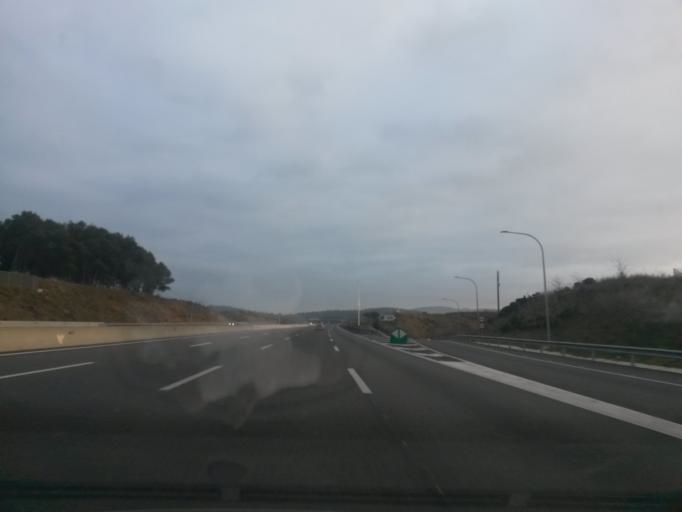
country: ES
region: Catalonia
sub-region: Provincia de Girona
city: Salt
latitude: 41.9916
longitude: 2.7906
